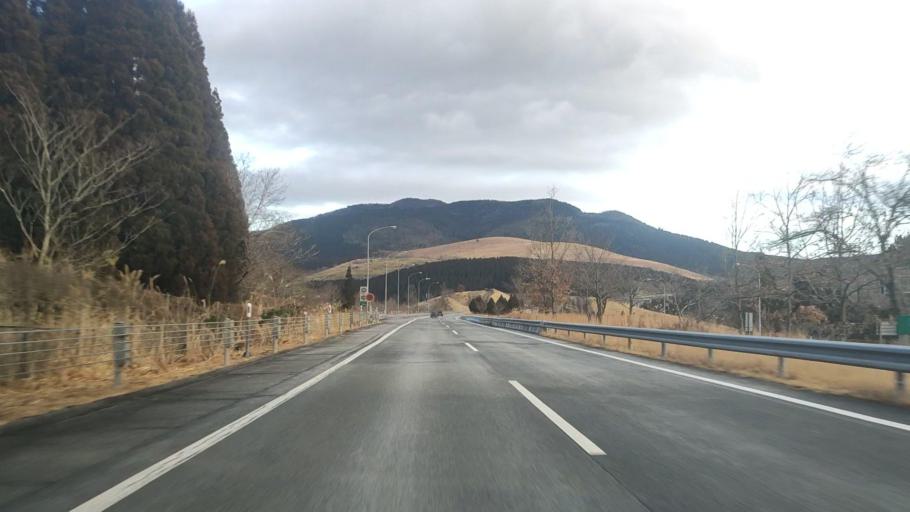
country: JP
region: Oita
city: Beppu
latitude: 33.2803
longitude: 131.3448
